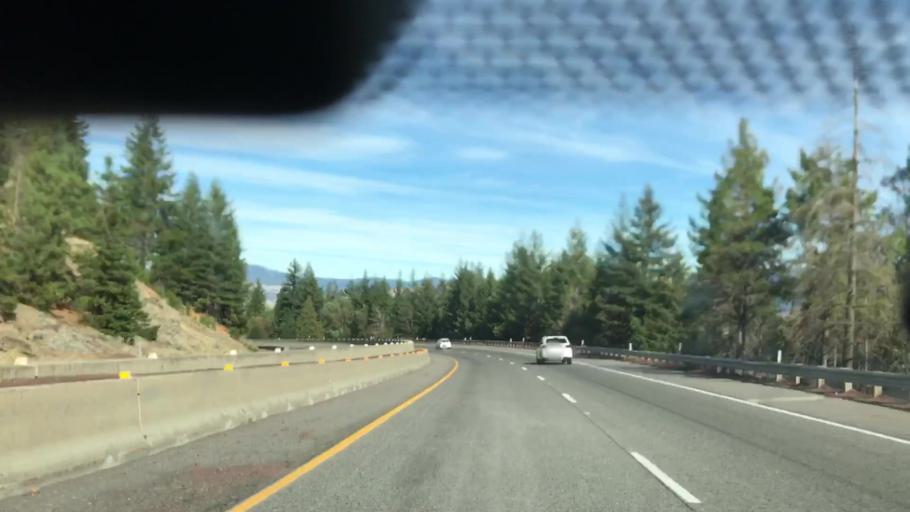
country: US
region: Oregon
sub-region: Jackson County
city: Ashland
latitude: 42.0814
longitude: -122.5994
